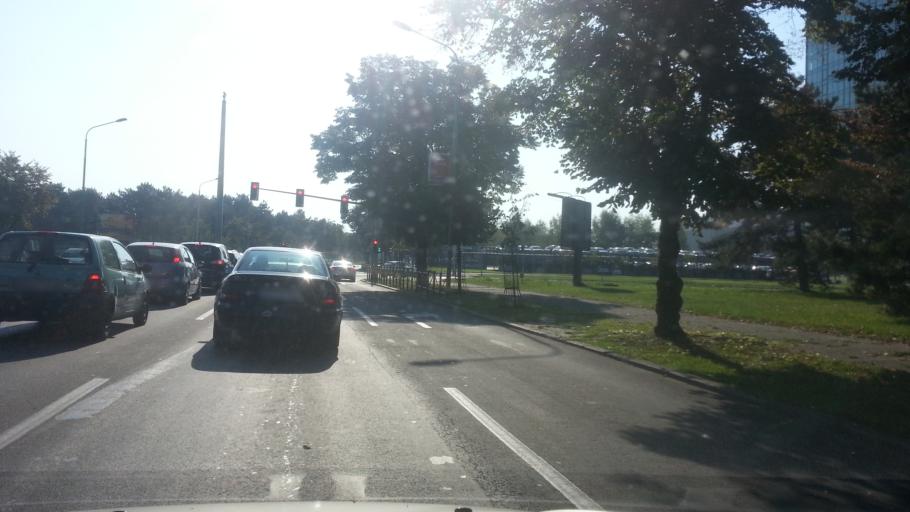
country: RS
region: Central Serbia
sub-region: Belgrade
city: Novi Beograd
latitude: 44.8180
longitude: 20.4365
